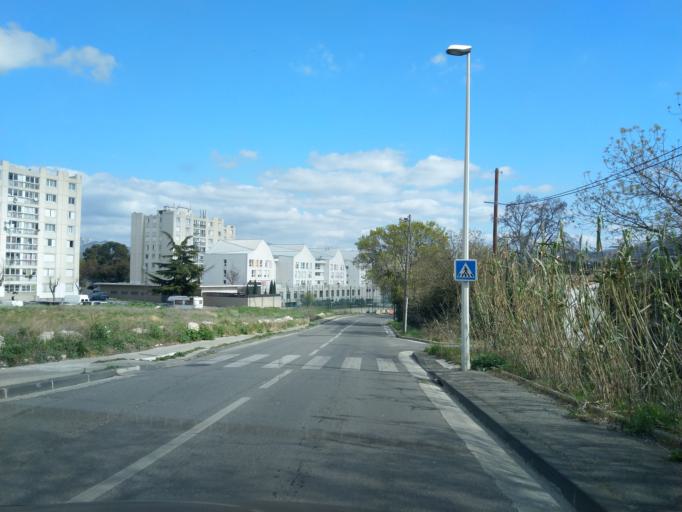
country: FR
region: Provence-Alpes-Cote d'Azur
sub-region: Departement des Bouches-du-Rhone
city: Plan-de-Cuques
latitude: 43.3280
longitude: 5.4546
